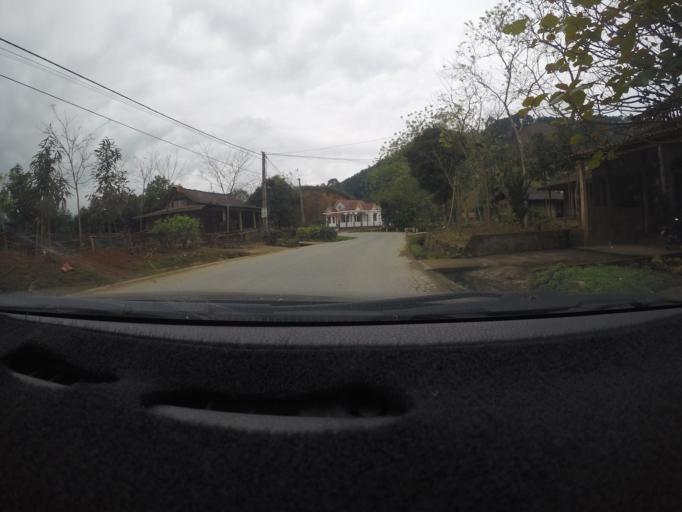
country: VN
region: Yen Bai
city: Co Phuc
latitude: 21.9255
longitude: 104.7970
